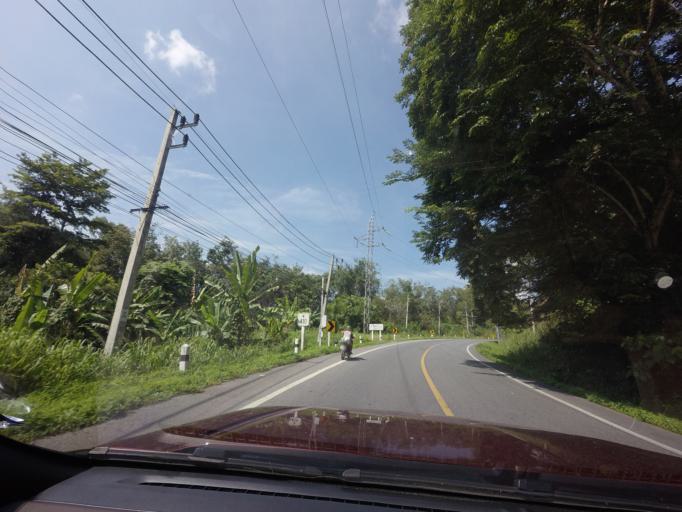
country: TH
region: Yala
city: Betong
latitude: 5.8643
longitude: 101.1278
